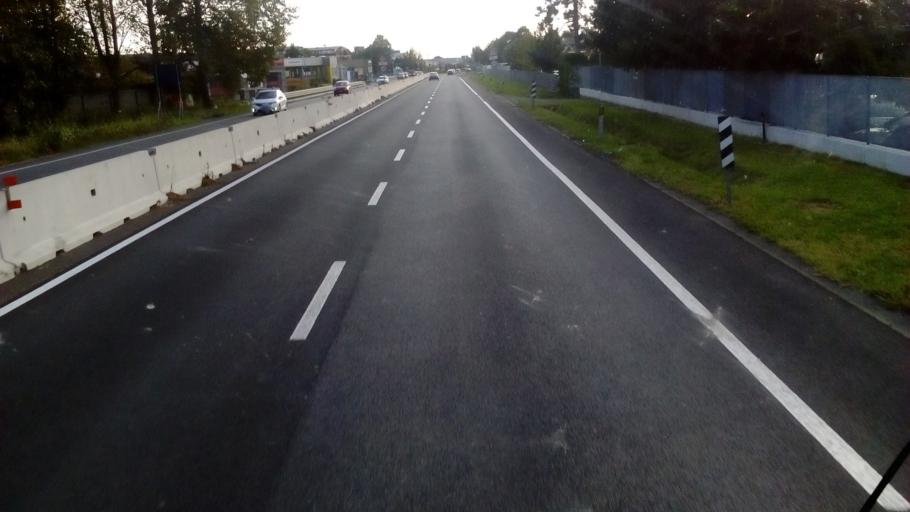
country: IT
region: Lombardy
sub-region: Provincia di Como
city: Novedrate
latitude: 45.6989
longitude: 9.1310
